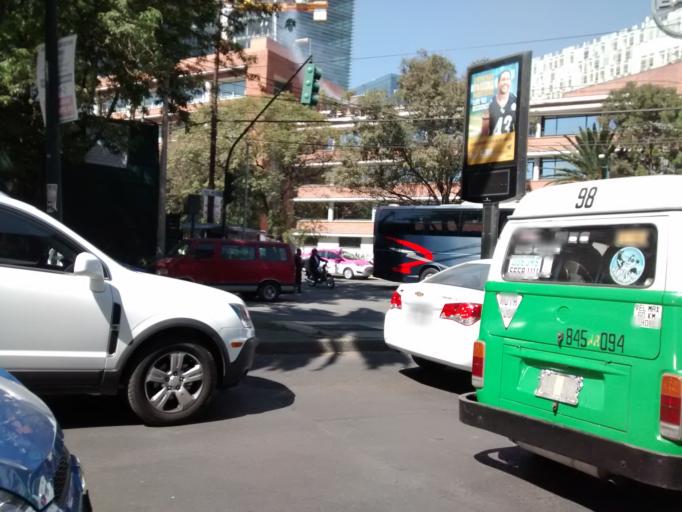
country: MX
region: Mexico City
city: Miguel Hidalgo
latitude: 19.4403
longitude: -99.2007
